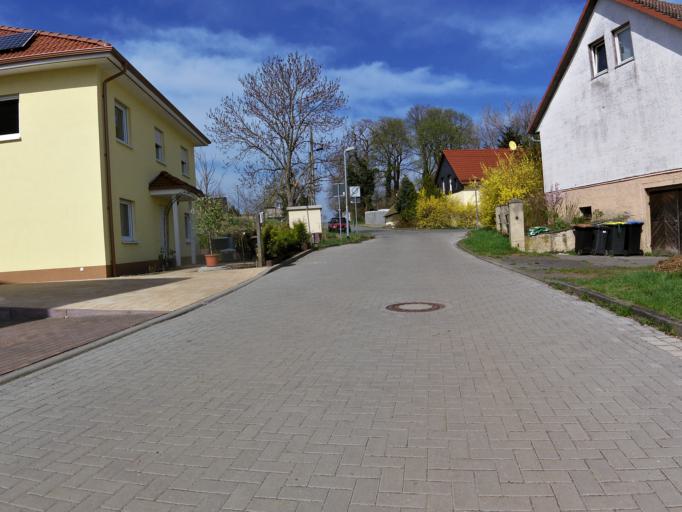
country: DE
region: Saxony
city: Schkeuditz
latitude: 51.3845
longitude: 12.2599
